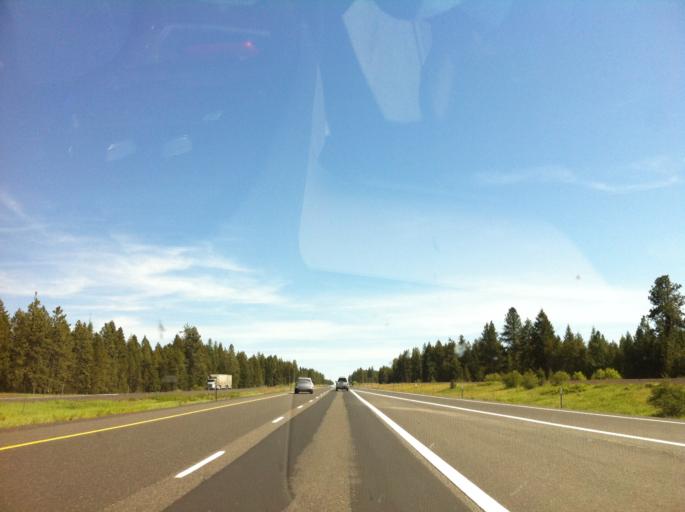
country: US
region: Oregon
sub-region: Umatilla County
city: Mission
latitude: 45.5059
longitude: -118.4257
